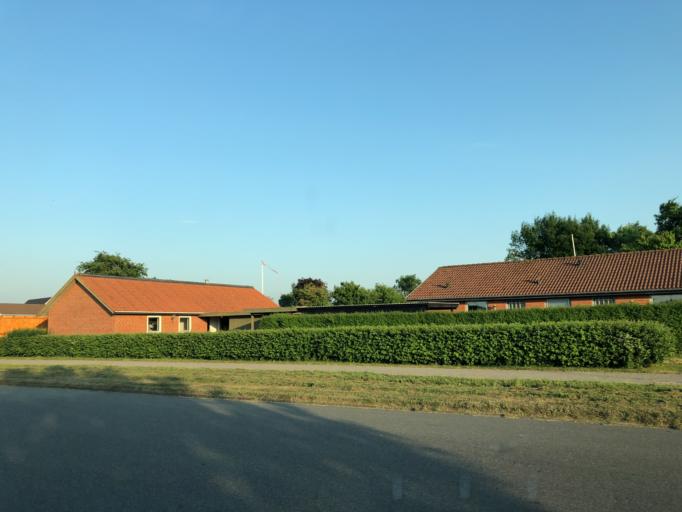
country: DK
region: Central Jutland
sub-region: Struer Kommune
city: Struer
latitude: 56.4809
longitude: 8.5579
